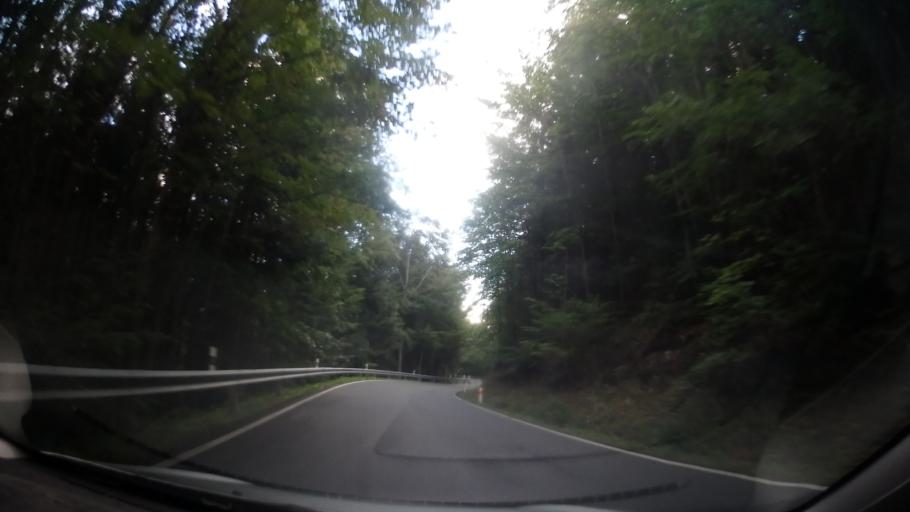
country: CZ
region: Olomoucky
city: Zabreh
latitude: 49.8857
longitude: 16.8108
